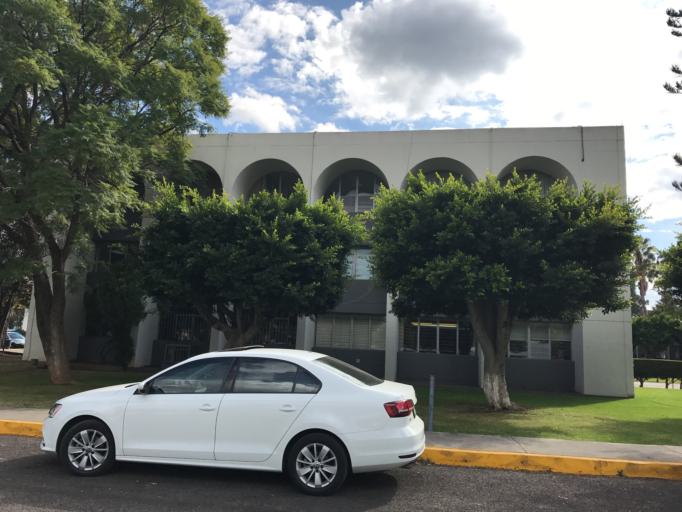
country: MX
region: Michoacan
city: Morelia
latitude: 19.6902
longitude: -101.2020
